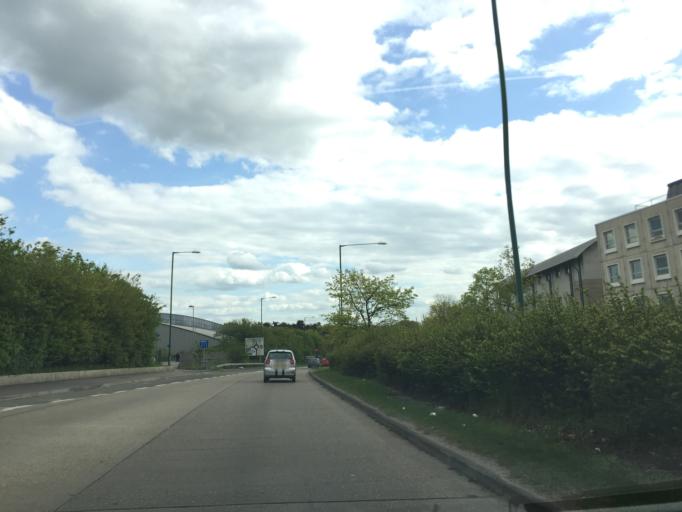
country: GB
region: England
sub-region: Essex
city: Harlow
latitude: 51.7695
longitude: 0.0973
